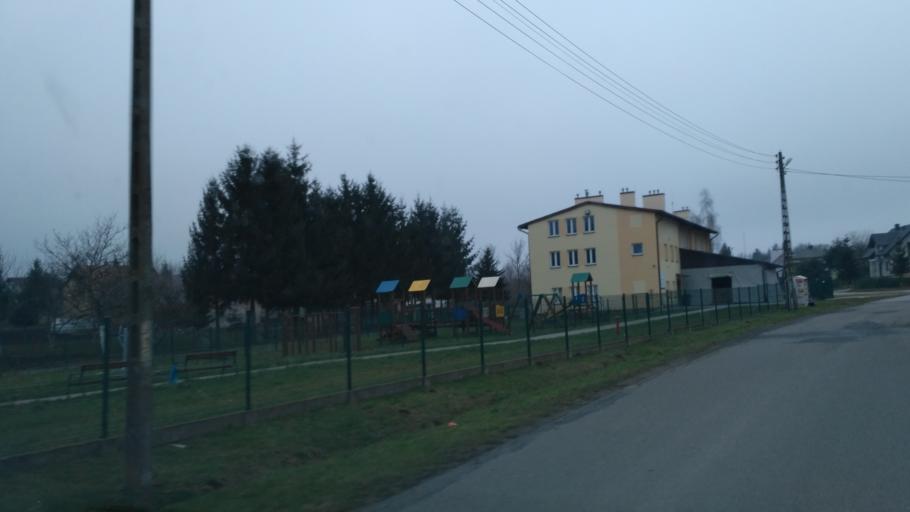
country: PL
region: Subcarpathian Voivodeship
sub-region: Powiat jaroslawski
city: Pawlosiow
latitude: 49.9638
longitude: 22.6501
